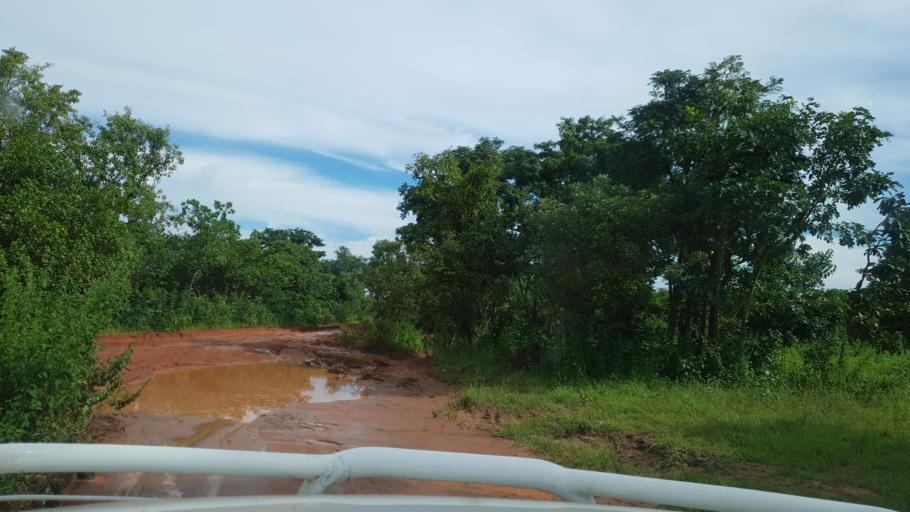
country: ML
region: Sikasso
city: Kolondieba
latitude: 10.7474
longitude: -6.9126
